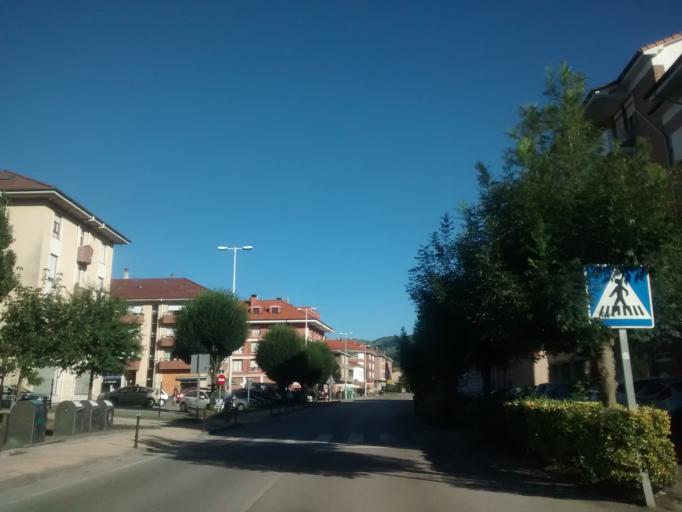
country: ES
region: Cantabria
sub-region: Provincia de Cantabria
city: Entrambasaguas
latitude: 43.3789
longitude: -3.6832
